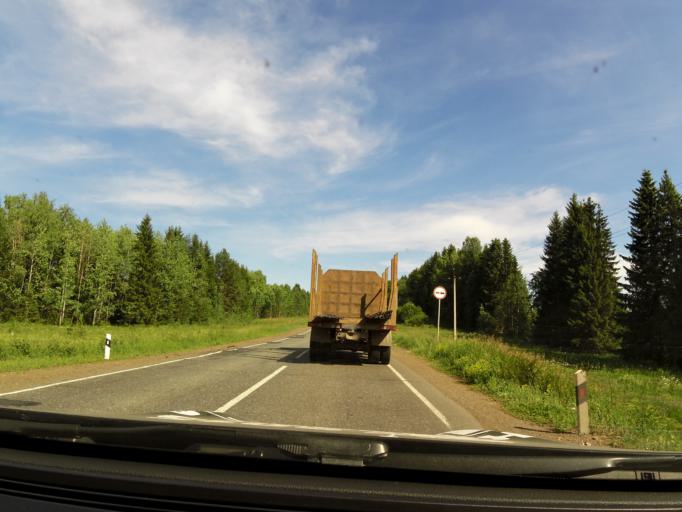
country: RU
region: Kirov
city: Belaya Kholunitsa
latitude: 58.8506
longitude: 50.7453
